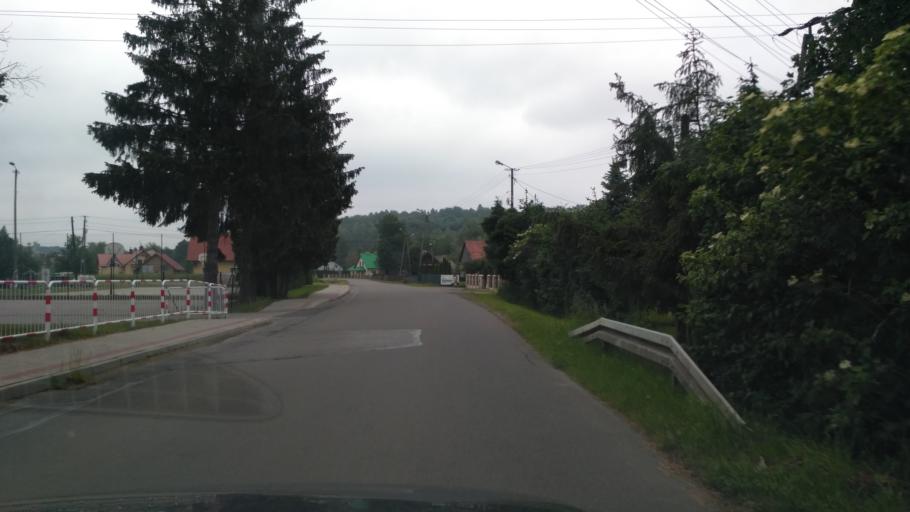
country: PL
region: Subcarpathian Voivodeship
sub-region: Powiat ropczycko-sedziszowski
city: Zagorzyce
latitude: 50.0184
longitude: 21.6769
